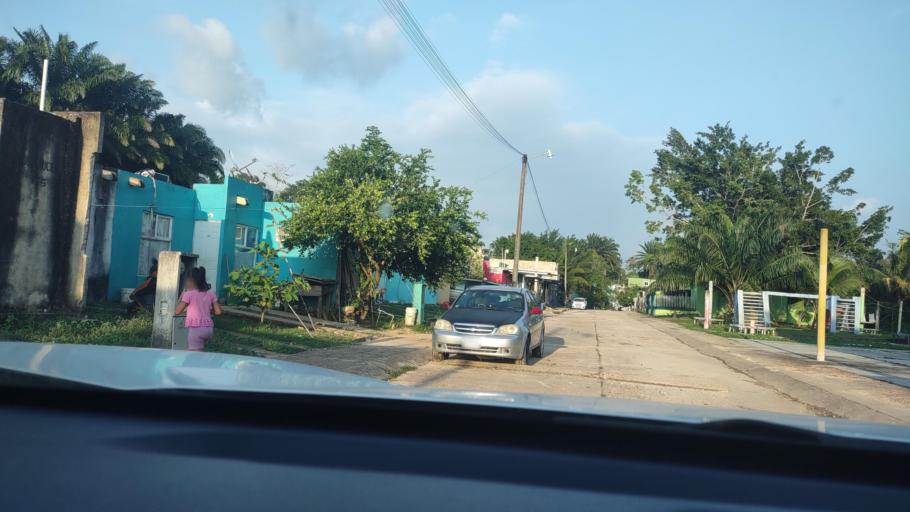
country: MX
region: Veracruz
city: Las Choapas
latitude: 17.9344
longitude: -94.1167
